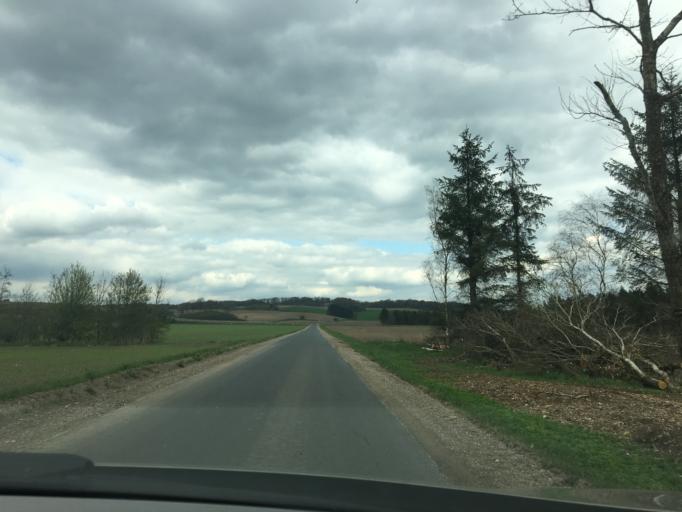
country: DK
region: Central Jutland
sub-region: Horsens Kommune
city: Braedstrup
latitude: 55.9529
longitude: 9.6656
